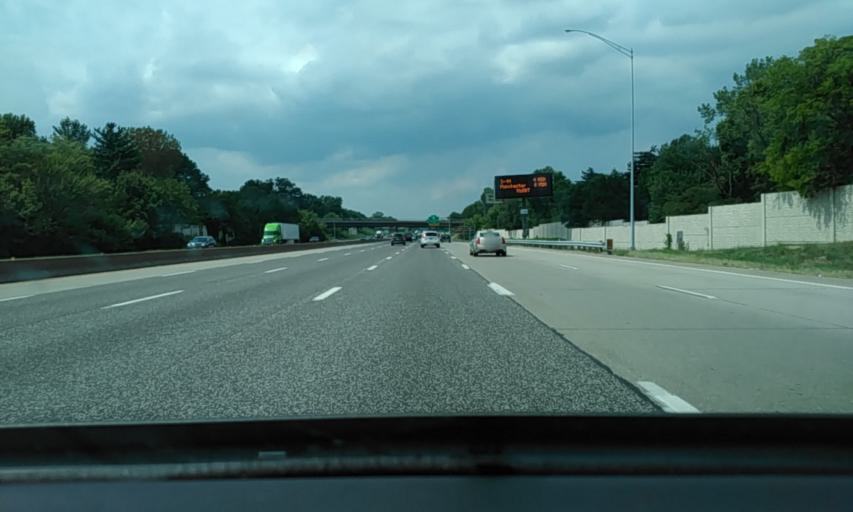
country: US
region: Missouri
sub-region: Saint Louis County
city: Concord
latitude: 38.5145
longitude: -90.3762
